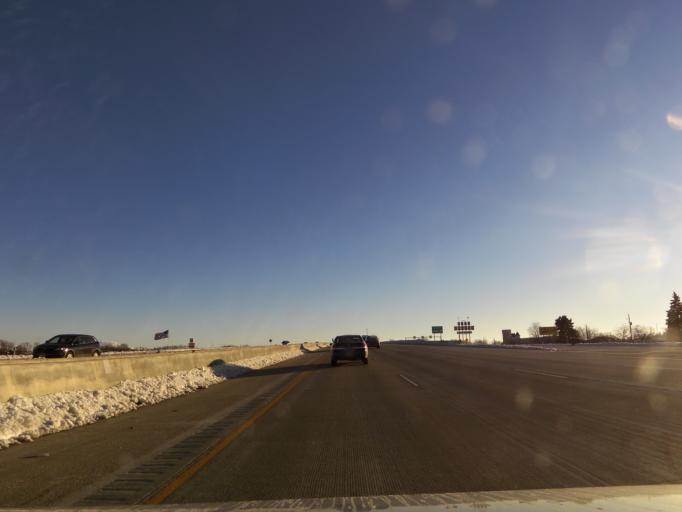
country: US
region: Wisconsin
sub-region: Kenosha County
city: Somers
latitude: 42.6186
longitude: -87.9525
